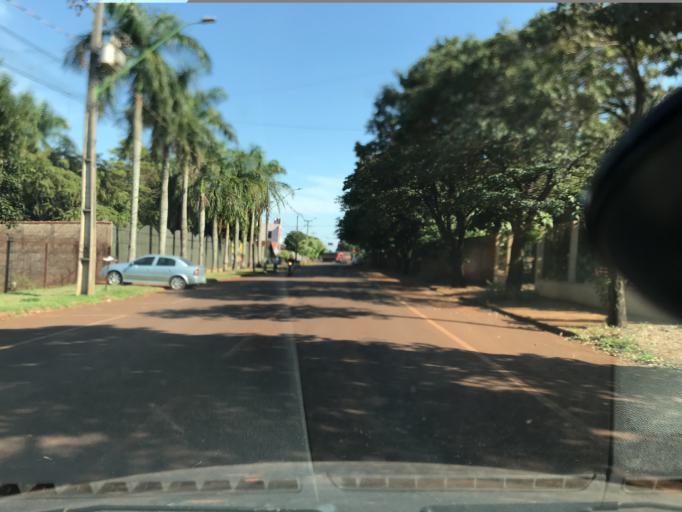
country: BR
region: Parana
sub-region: Palotina
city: Palotina
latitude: -24.2931
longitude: -53.8442
